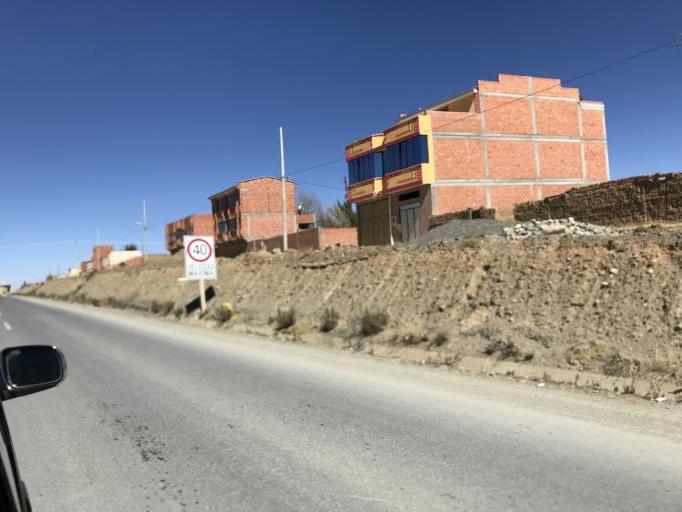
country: BO
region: La Paz
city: Batallas
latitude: -16.3340
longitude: -68.4177
